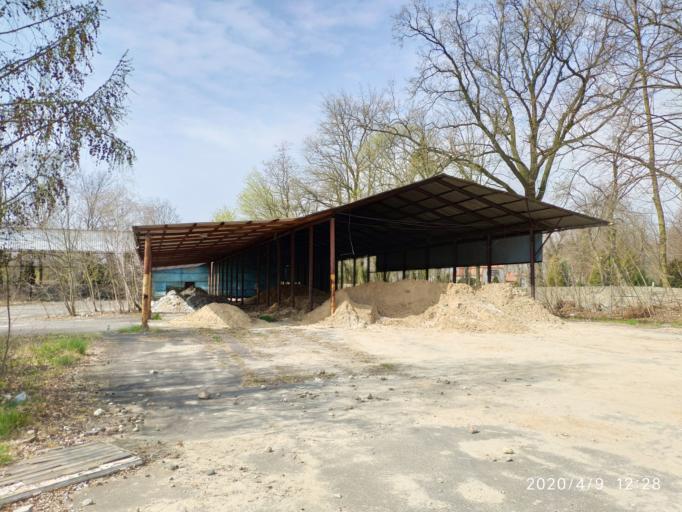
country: PL
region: Lubusz
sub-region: Powiat zielonogorski
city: Sulechow
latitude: 52.0830
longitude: 15.6153
